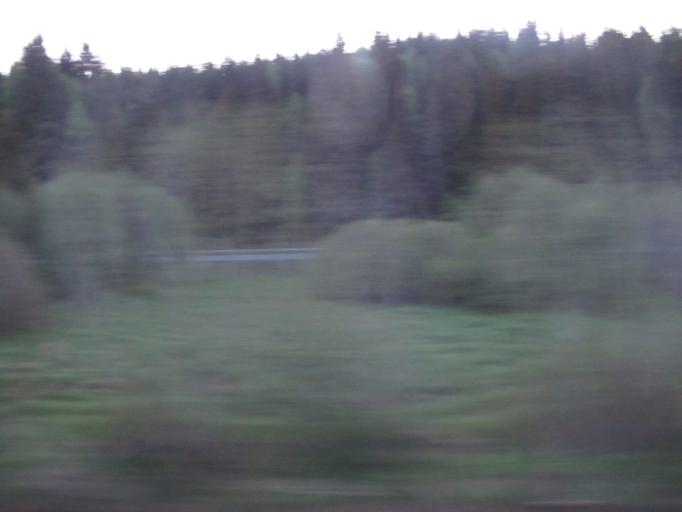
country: NO
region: Oppland
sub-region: Ringebu
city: Ringebu
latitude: 61.5353
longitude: 10.1062
